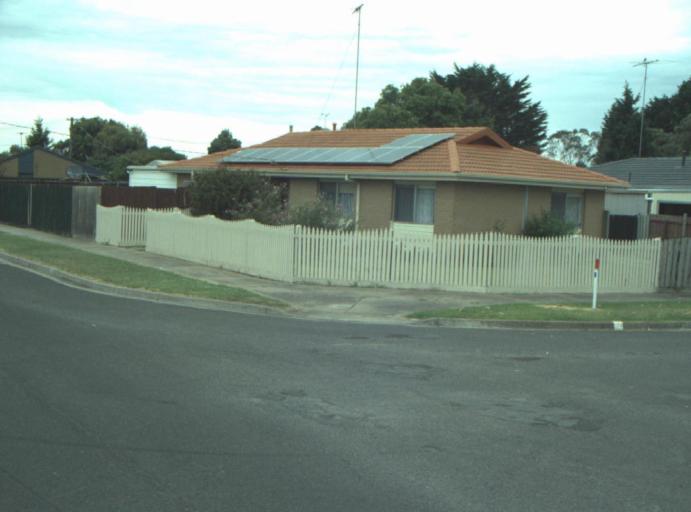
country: AU
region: Victoria
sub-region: Greater Geelong
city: Breakwater
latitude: -38.1800
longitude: 144.3981
